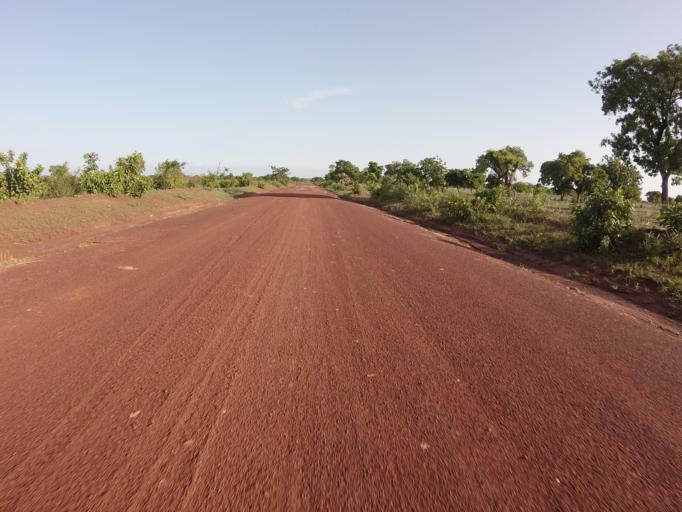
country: TG
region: Savanes
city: Sansanne-Mango
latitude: 10.3792
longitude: -0.0946
